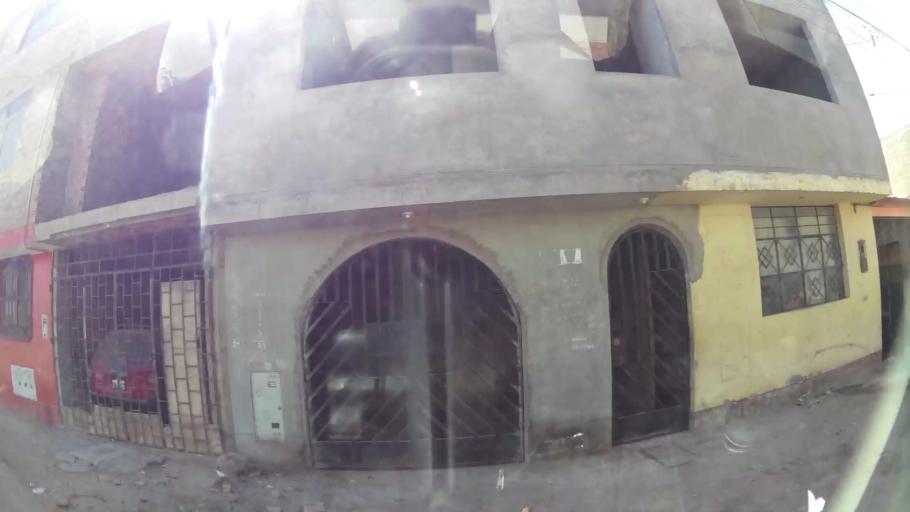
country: PE
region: Ica
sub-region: Provincia de Ica
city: Subtanjalla
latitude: -14.0427
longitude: -75.7503
